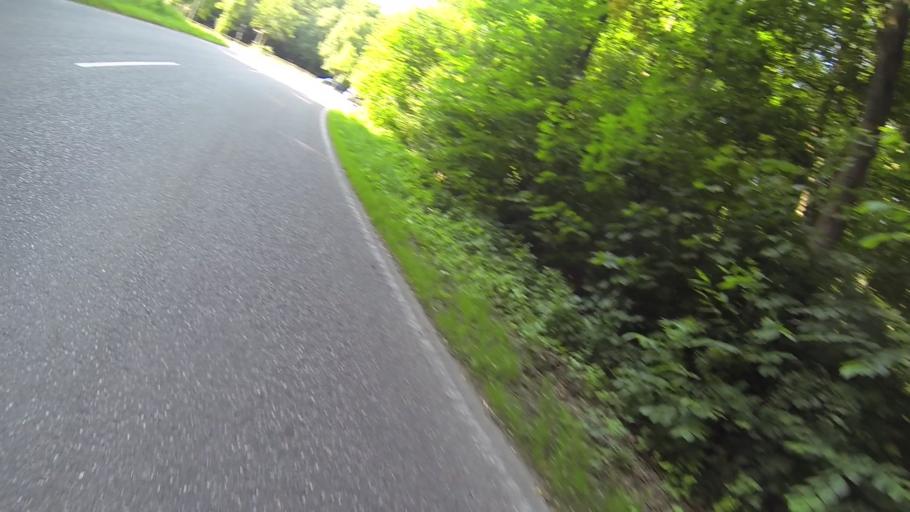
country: DE
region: Bavaria
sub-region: Swabia
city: Neu-Ulm
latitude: 48.4182
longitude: 10.0246
